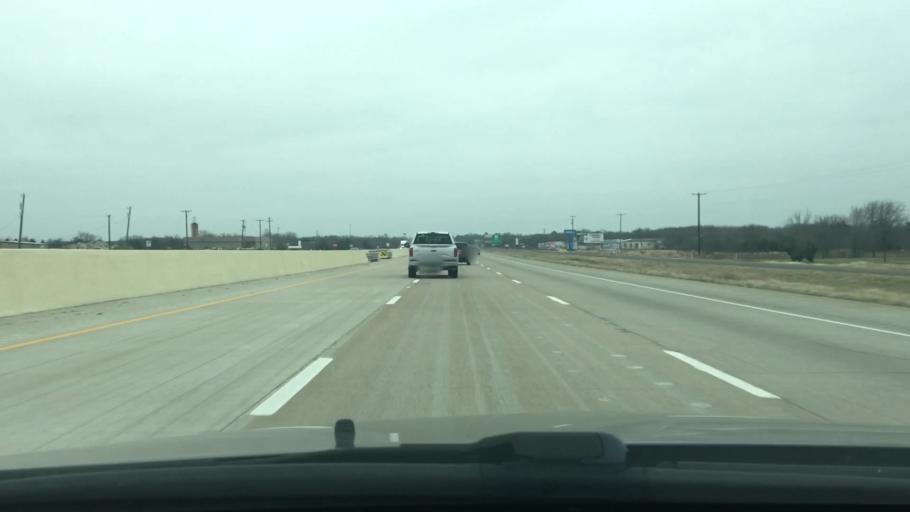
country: US
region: Texas
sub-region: Navarro County
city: Corsicana
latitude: 32.0276
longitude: -96.4418
